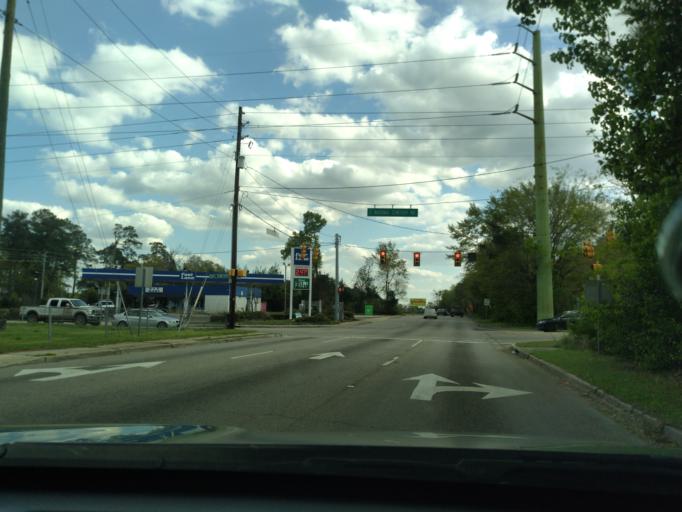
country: US
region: South Carolina
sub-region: Florence County
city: Florence
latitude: 34.1847
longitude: -79.7623
